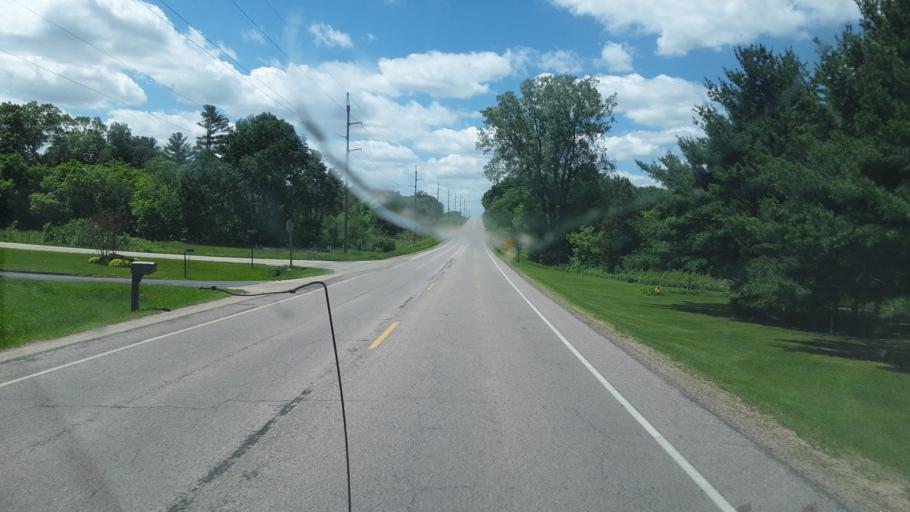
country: US
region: Wisconsin
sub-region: Sauk County
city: Lake Delton
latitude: 43.5906
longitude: -89.8364
